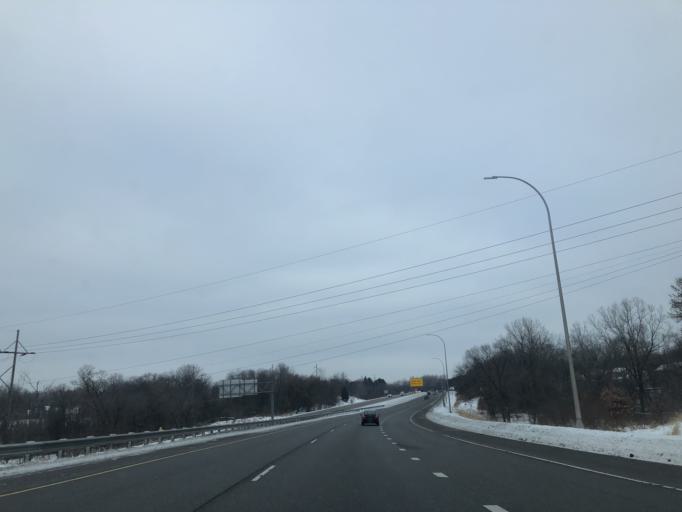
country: US
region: Minnesota
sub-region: Ramsey County
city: Arden Hills
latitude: 45.0677
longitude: -93.1665
